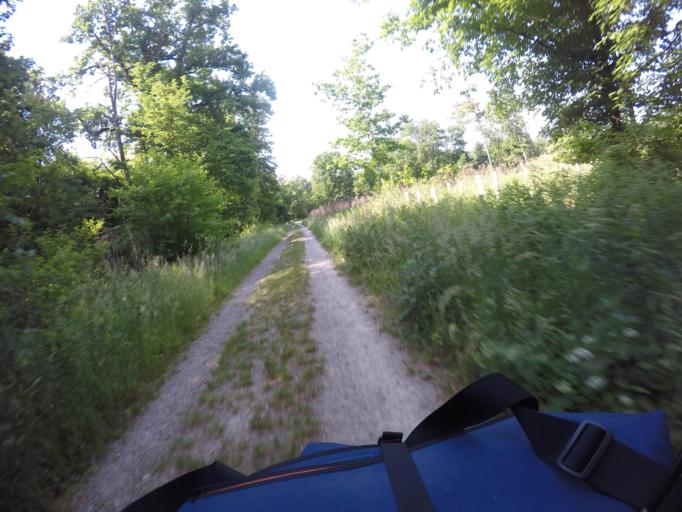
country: DE
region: Baden-Wuerttemberg
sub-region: Karlsruhe Region
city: Rheinstetten
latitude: 48.9327
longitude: 8.3064
